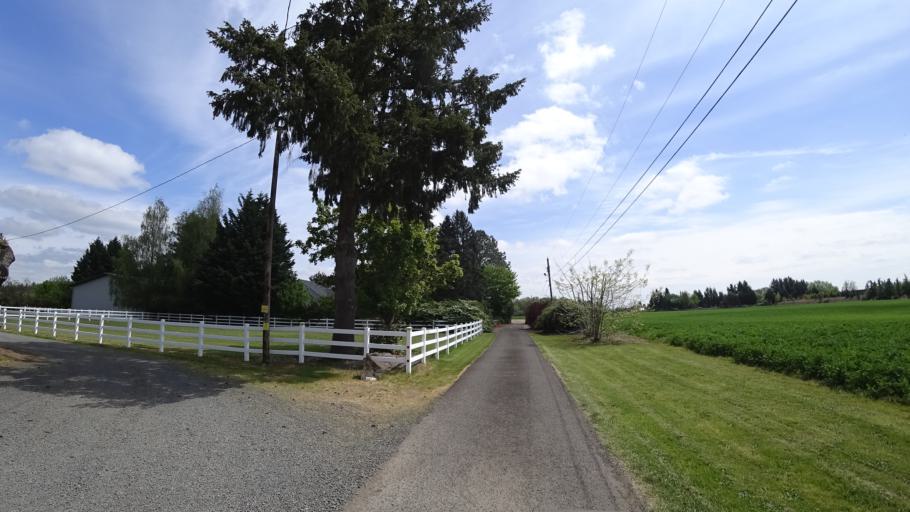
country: US
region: Oregon
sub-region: Washington County
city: Hillsboro
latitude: 45.5534
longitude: -122.9935
